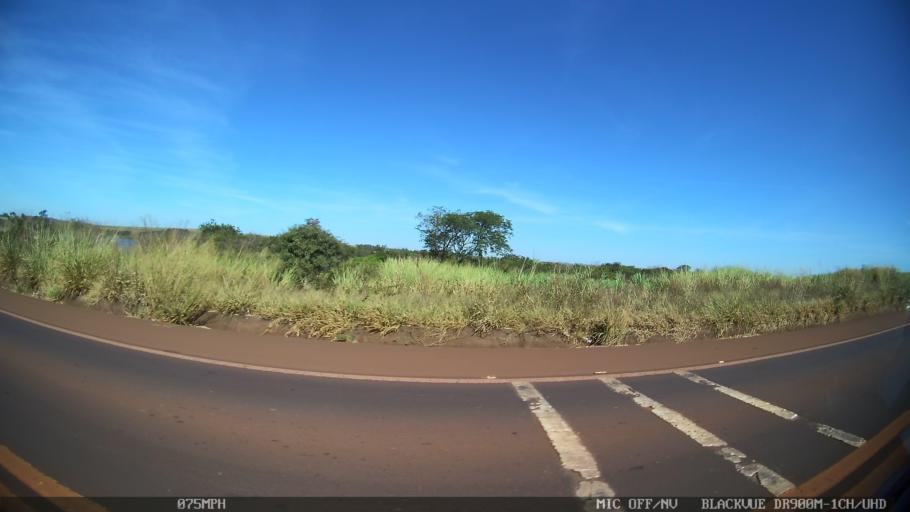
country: BR
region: Sao Paulo
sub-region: Sao Joaquim Da Barra
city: Sao Joaquim da Barra
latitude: -20.5401
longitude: -47.8133
